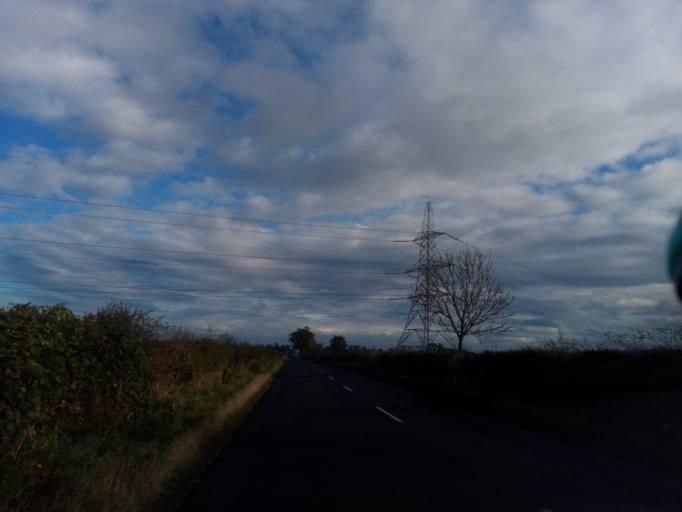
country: GB
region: Scotland
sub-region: The Scottish Borders
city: Duns
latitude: 55.6776
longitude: -2.3601
